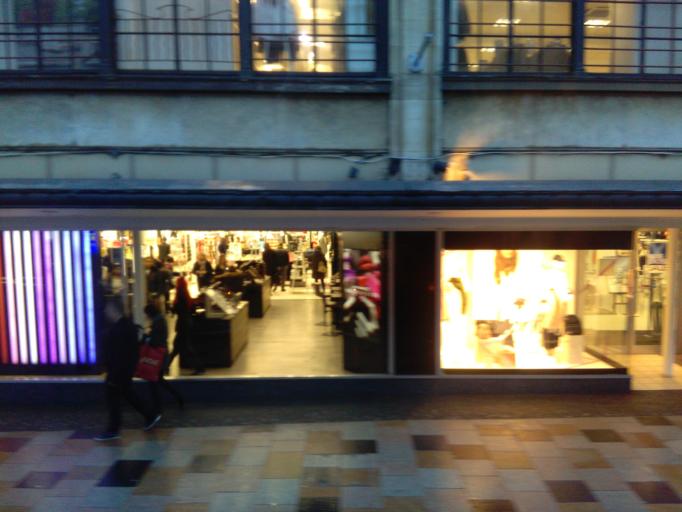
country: GB
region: England
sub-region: Greater London
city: Battersea
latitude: 51.4633
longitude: -0.1678
